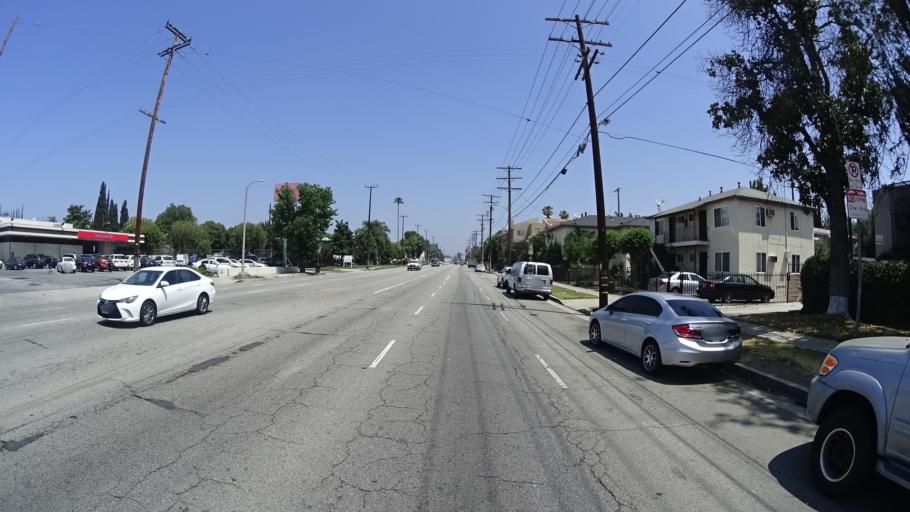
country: US
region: California
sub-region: Los Angeles County
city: Van Nuys
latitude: 34.2024
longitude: -118.4308
